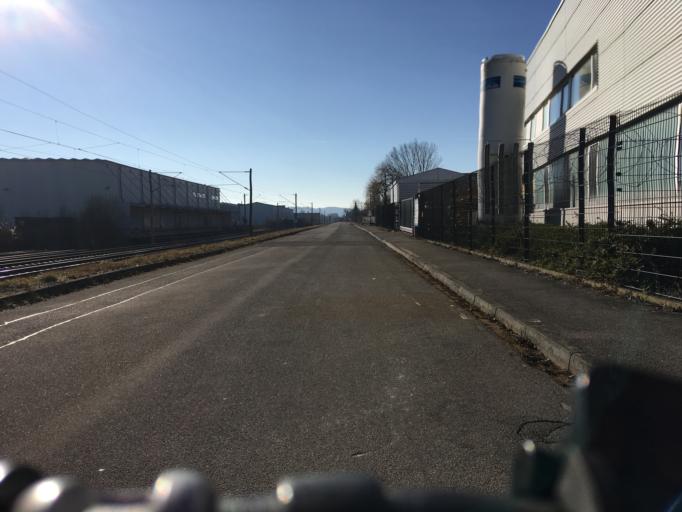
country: DE
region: Baden-Wuerttemberg
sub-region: Freiburg Region
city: Gottmadingen
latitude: 47.7404
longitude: 8.7913
